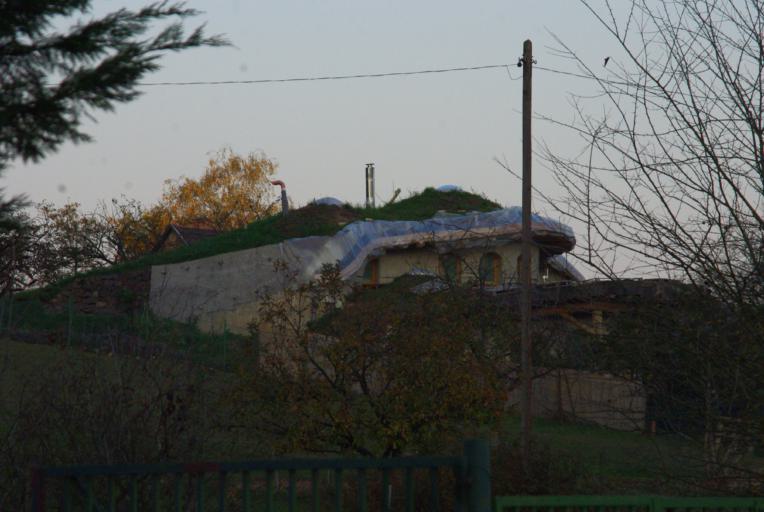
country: HU
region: Pest
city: Pilisszentivan
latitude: 47.6143
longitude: 18.8713
